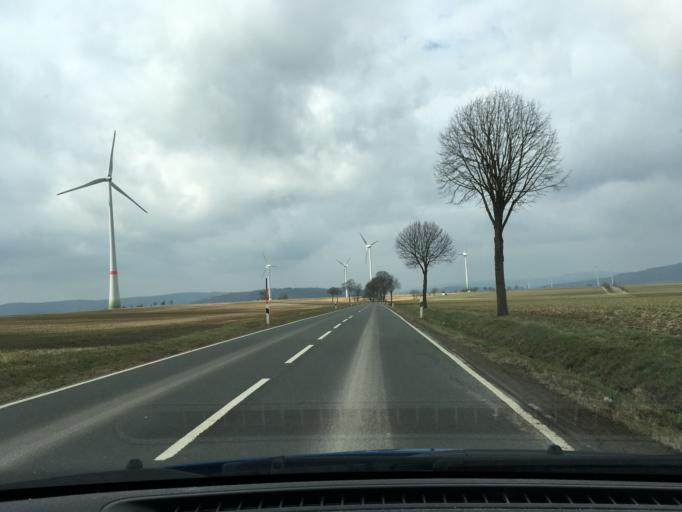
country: DE
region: Lower Saxony
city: Dransfeld
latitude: 51.5071
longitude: 9.7518
